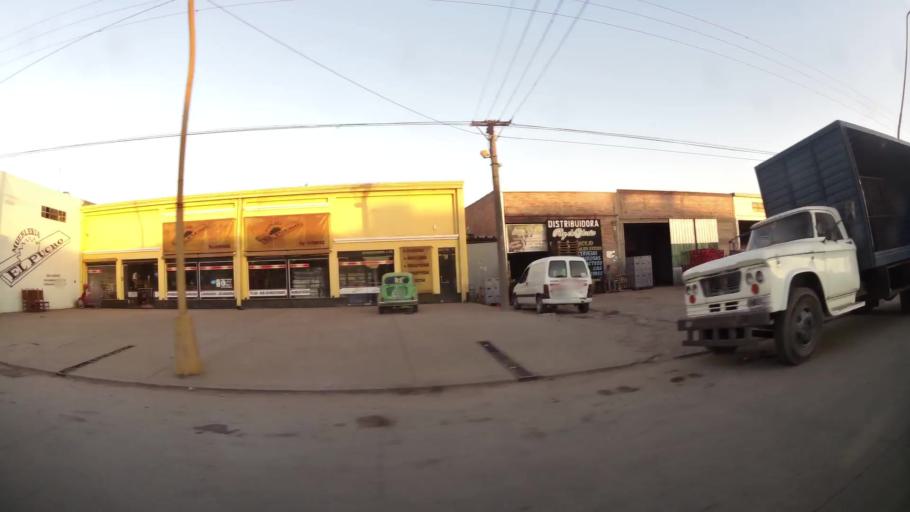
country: AR
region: Santa Fe
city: Santa Fe de la Vera Cruz
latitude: -31.5900
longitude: -60.6982
